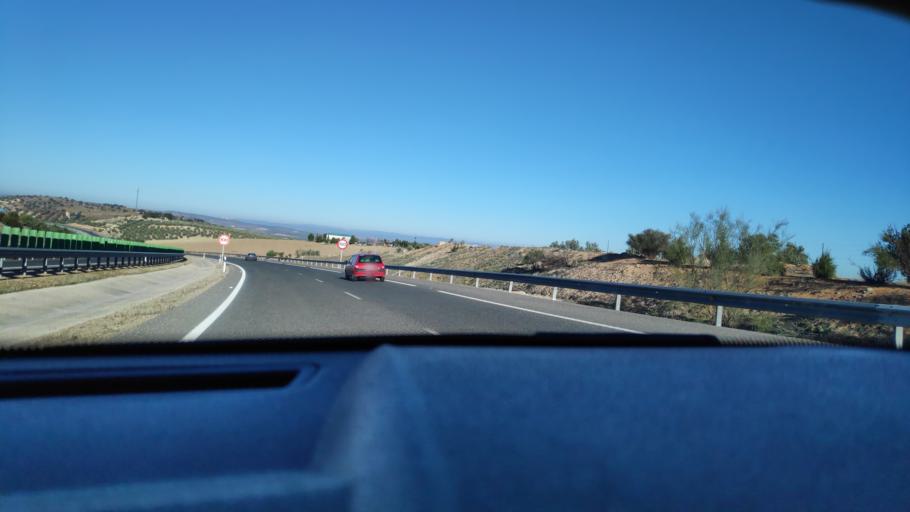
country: ES
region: Andalusia
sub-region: Provincia de Jaen
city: Jaen
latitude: 37.8156
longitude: -3.7364
